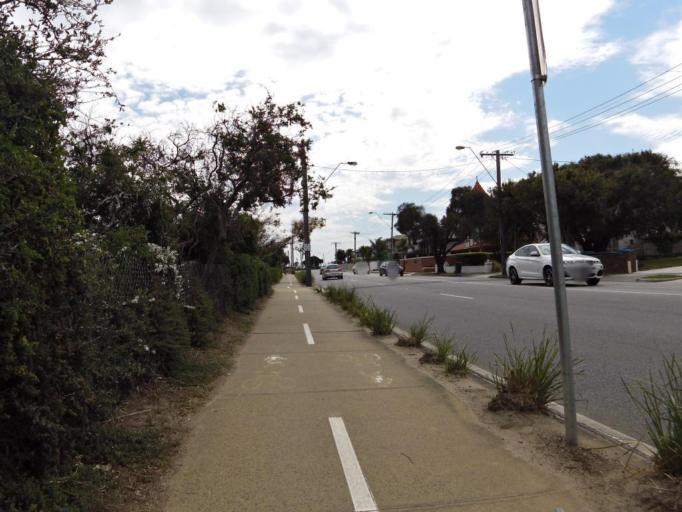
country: AU
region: Victoria
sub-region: Bayside
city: North Brighton
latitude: -37.9187
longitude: 144.9878
